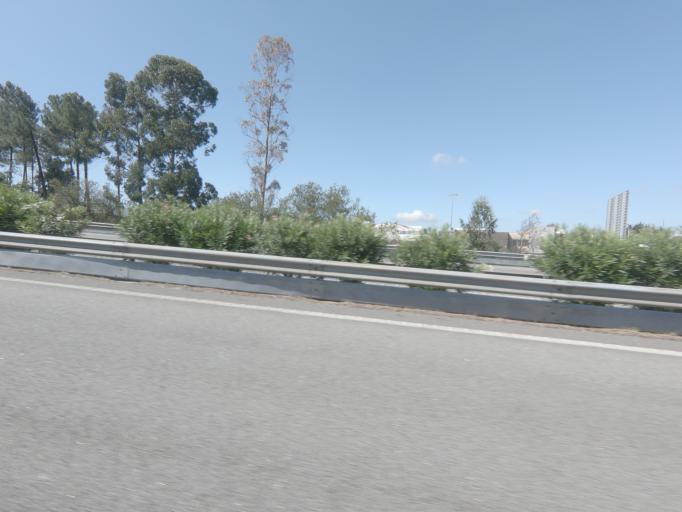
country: PT
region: Porto
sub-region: Paredes
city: Gandra
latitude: 41.1758
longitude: -8.4402
